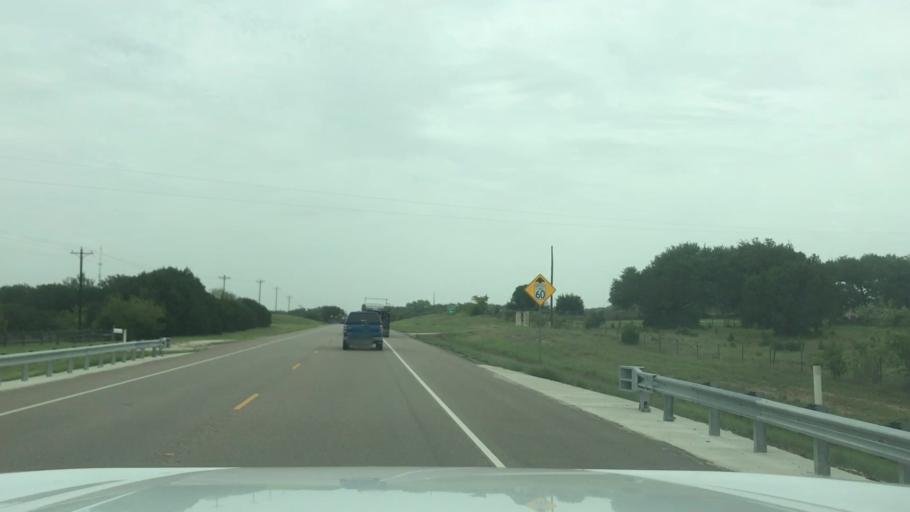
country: US
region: Texas
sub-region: Bosque County
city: Meridian
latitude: 31.9237
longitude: -97.6803
